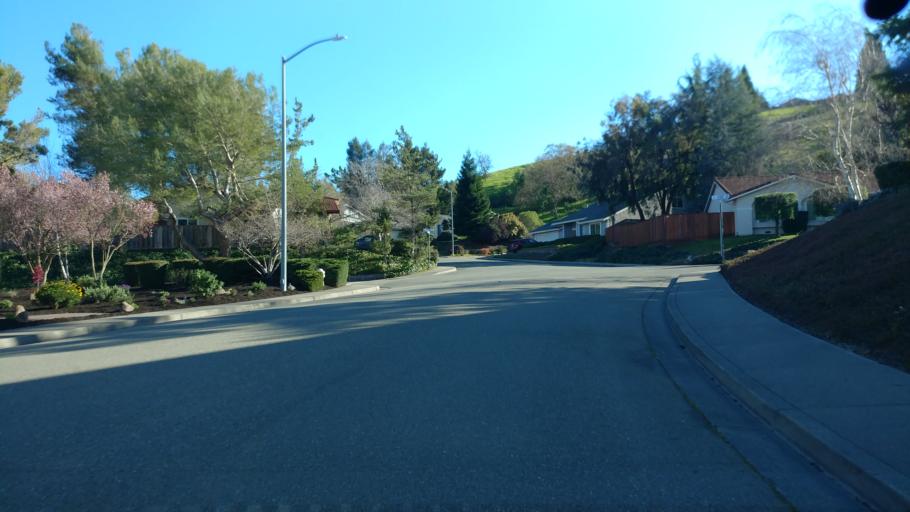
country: US
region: California
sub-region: Contra Costa County
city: San Ramon
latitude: 37.7589
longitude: -121.9785
